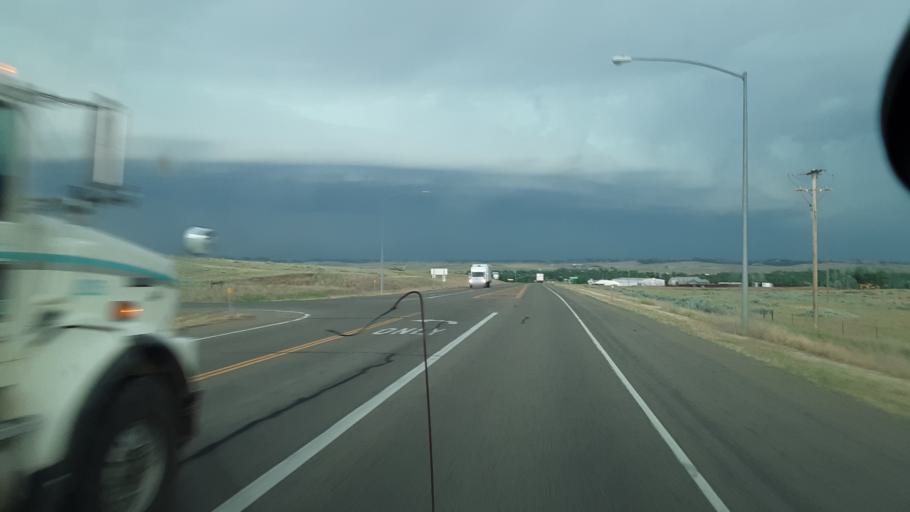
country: US
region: Montana
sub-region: Powder River County
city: Broadus
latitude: 45.4229
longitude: -105.3967
